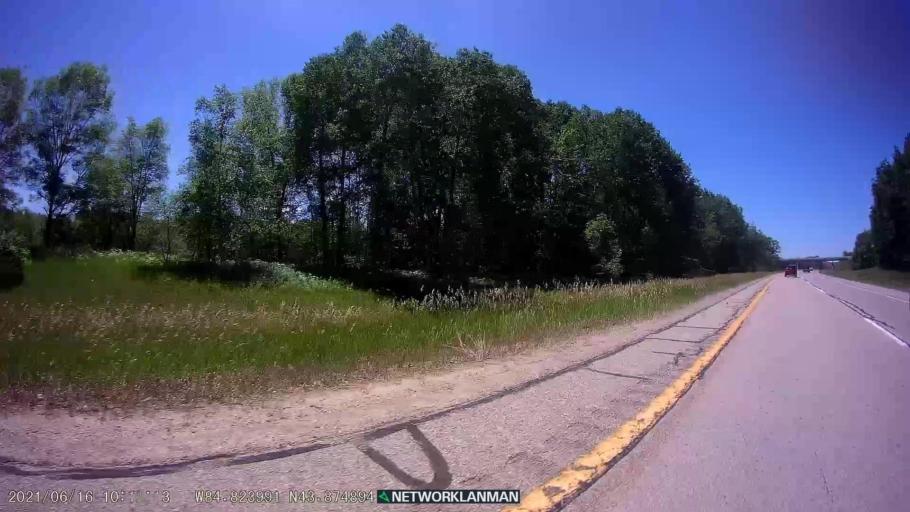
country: US
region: Michigan
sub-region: Clare County
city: Clare
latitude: 43.8756
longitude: -84.8254
